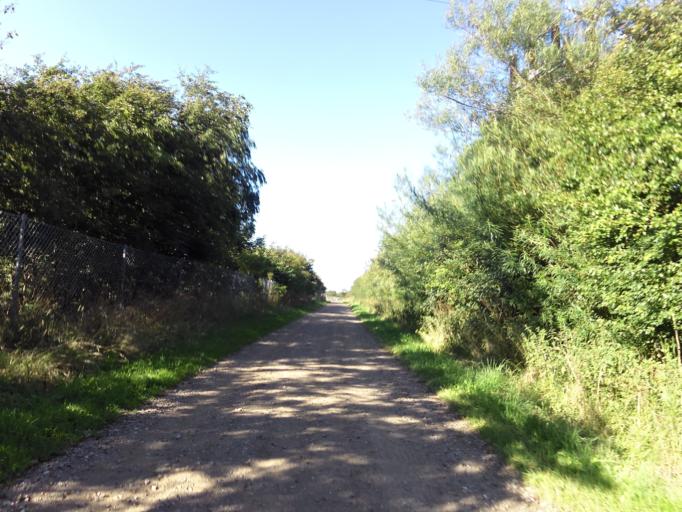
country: DK
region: South Denmark
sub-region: Tonder Kommune
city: Sherrebek
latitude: 55.1542
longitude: 8.7434
